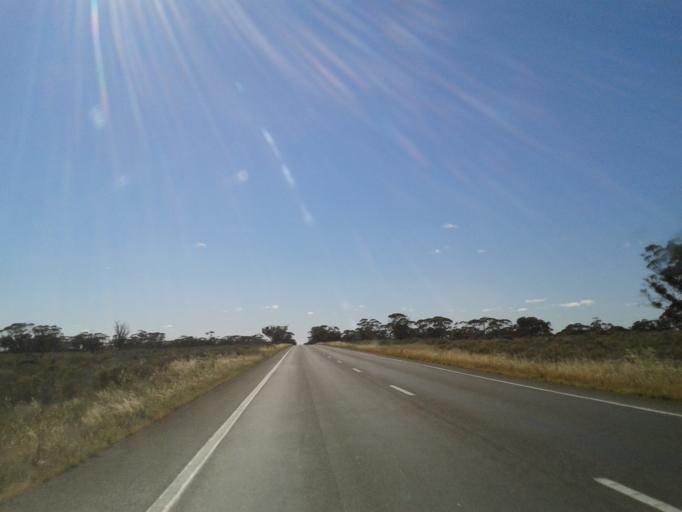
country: AU
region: South Australia
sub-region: Renmark Paringa
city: Renmark
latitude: -34.2744
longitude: 141.0419
